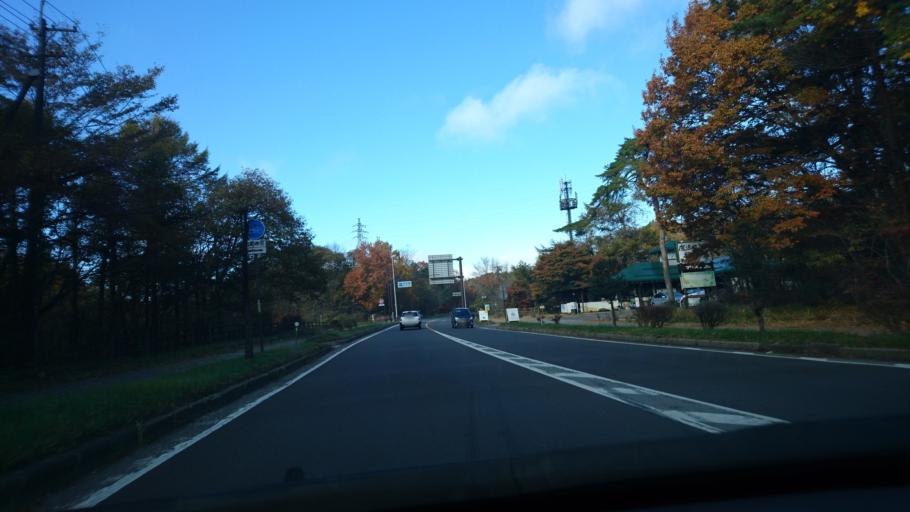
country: JP
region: Nagano
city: Saku
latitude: 36.3237
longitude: 138.6258
